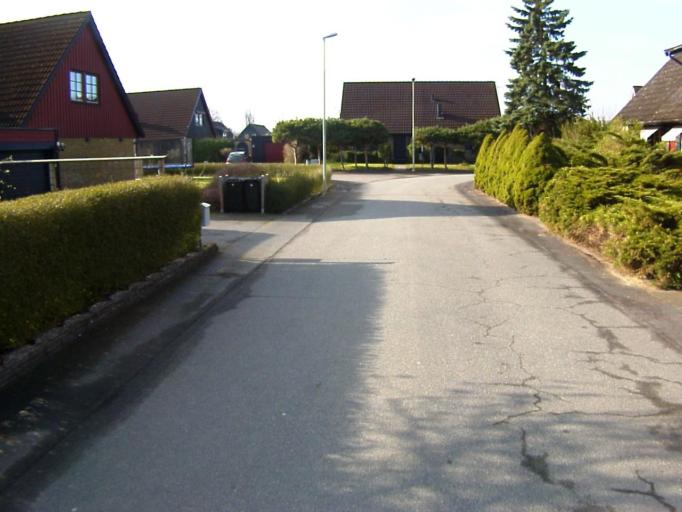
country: SE
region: Skane
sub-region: Kristianstads Kommun
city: Kristianstad
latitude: 56.0135
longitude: 14.1072
